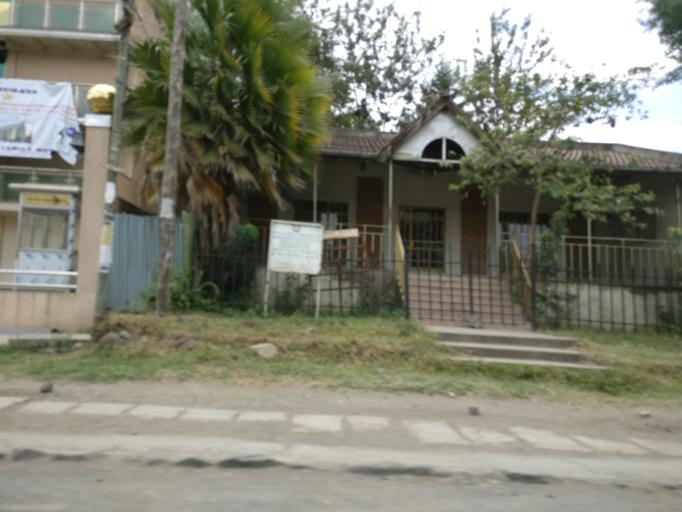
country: ET
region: Oromiya
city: Bishoftu
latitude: 8.7517
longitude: 38.9571
